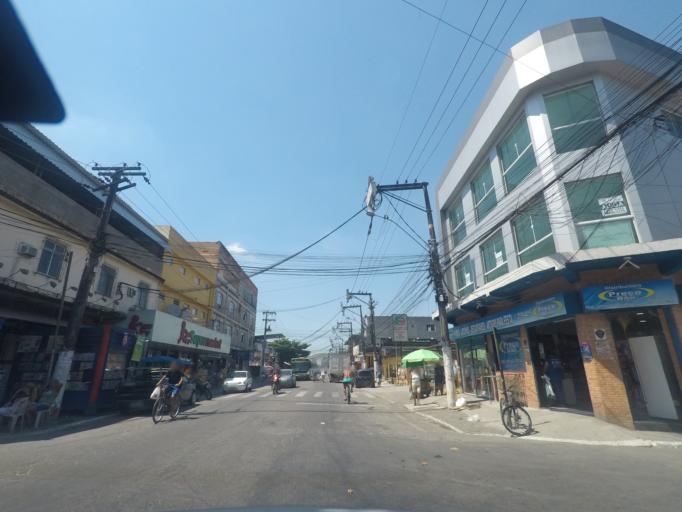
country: BR
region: Rio de Janeiro
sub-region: Petropolis
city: Petropolis
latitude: -22.5889
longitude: -43.1862
